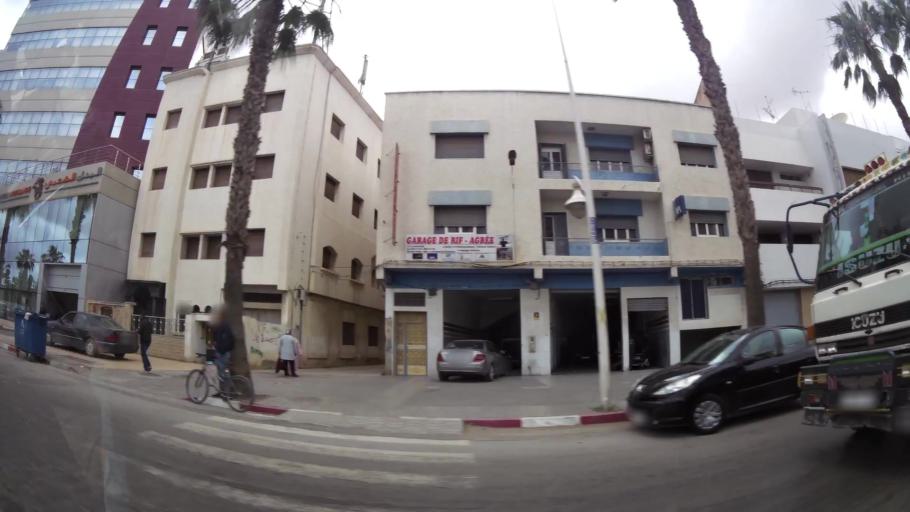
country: MA
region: Oriental
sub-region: Nador
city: Nador
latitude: 35.1609
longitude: -2.9309
